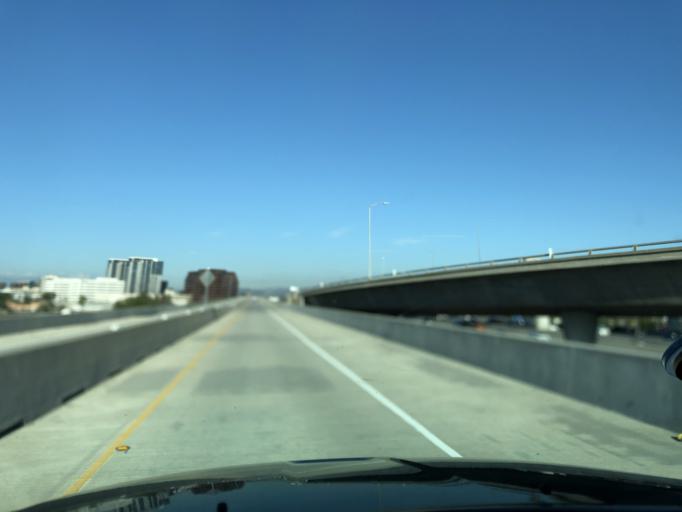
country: US
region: California
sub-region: Orange County
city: Irvine
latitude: 33.6897
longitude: -117.8705
